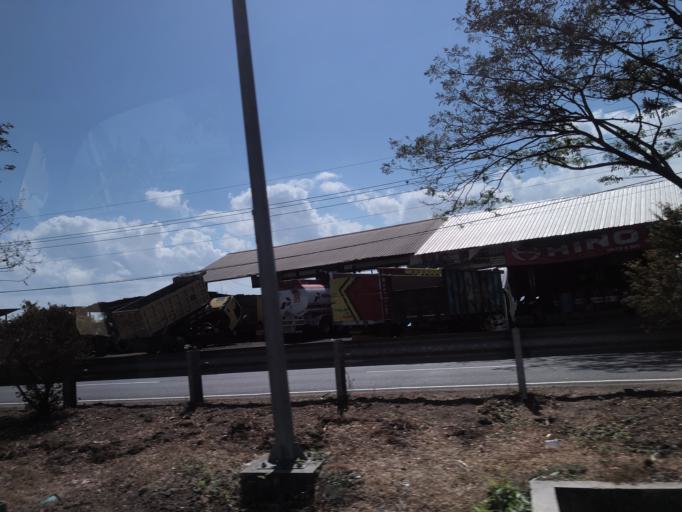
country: ID
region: Bali
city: Semarapura
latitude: -8.5679
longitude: 115.4109
